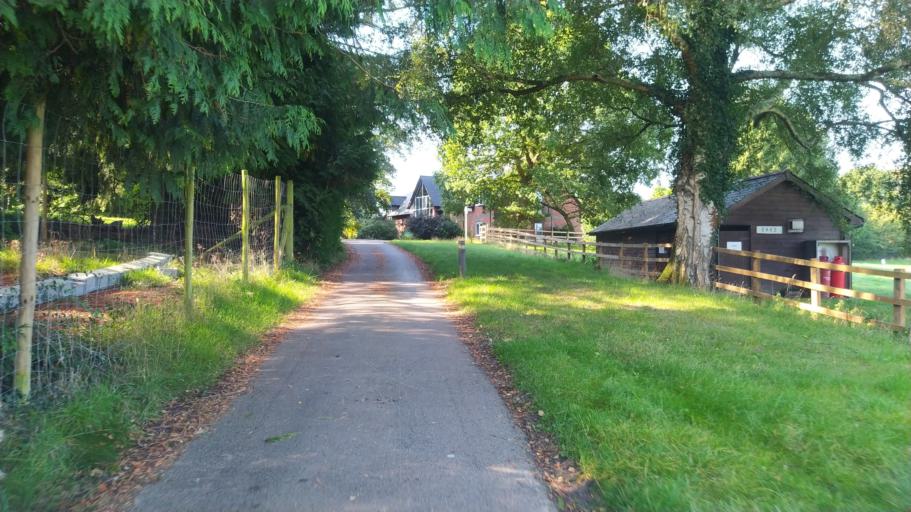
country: GB
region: England
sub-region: Hampshire
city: Lyndhurst
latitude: 50.8615
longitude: -1.5777
